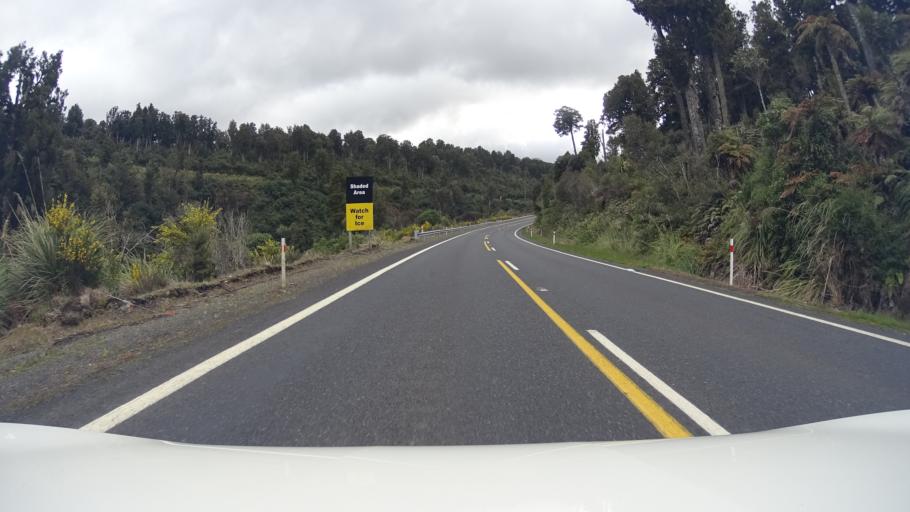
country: NZ
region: Manawatu-Wanganui
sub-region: Ruapehu District
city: Waiouru
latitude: -39.2658
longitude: 175.3926
